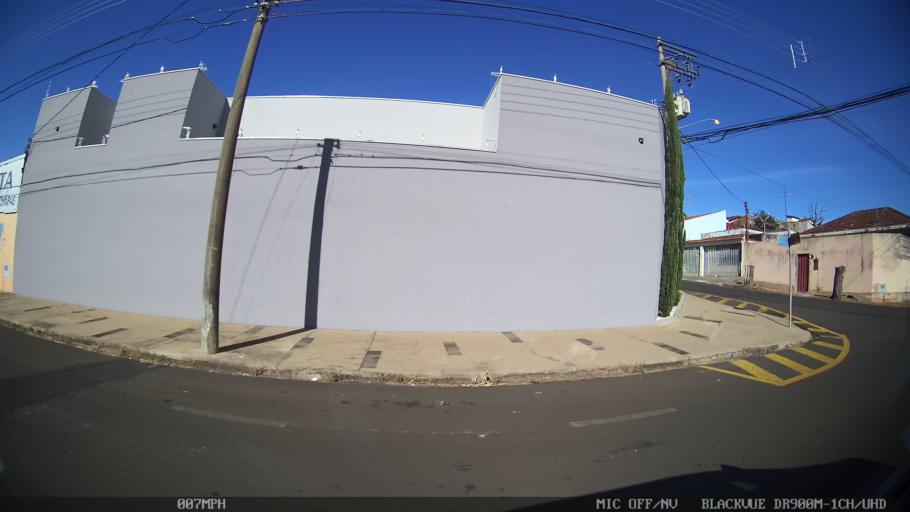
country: BR
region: Sao Paulo
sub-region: Franca
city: Franca
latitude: -20.5312
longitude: -47.4089
